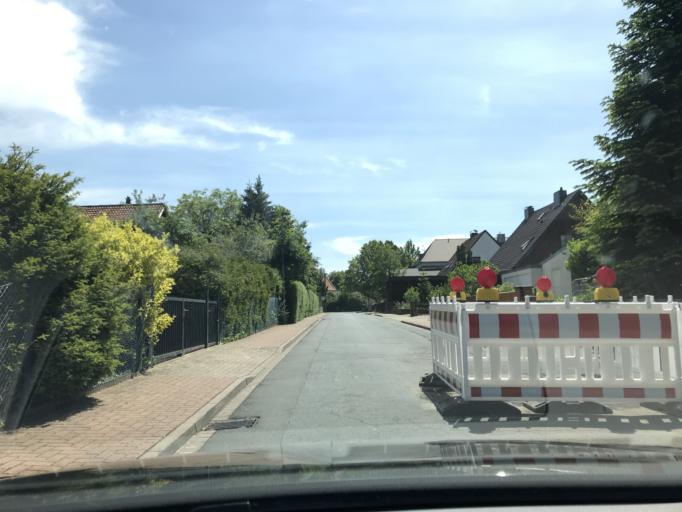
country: DE
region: Lower Saxony
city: Sehnde
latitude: 52.3470
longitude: 9.9369
